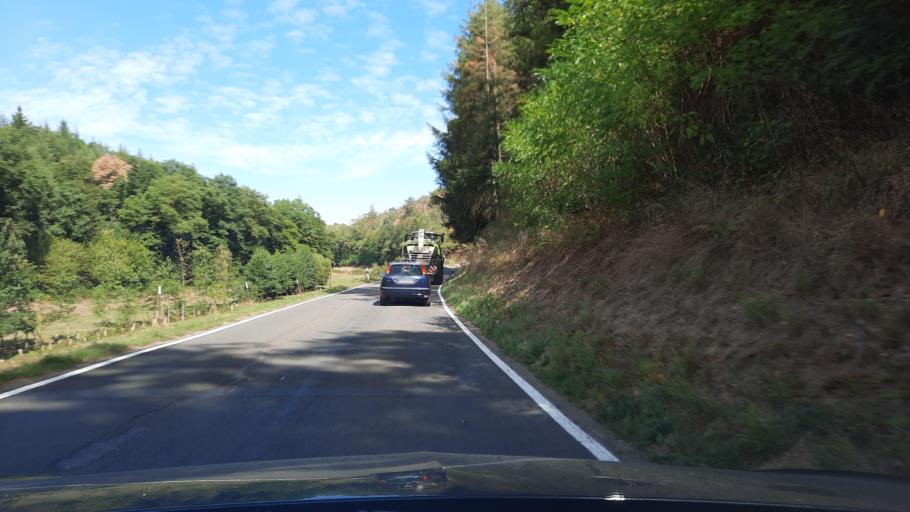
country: DE
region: Rheinland-Pfalz
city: Saarburg
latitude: 49.6209
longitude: 6.5324
